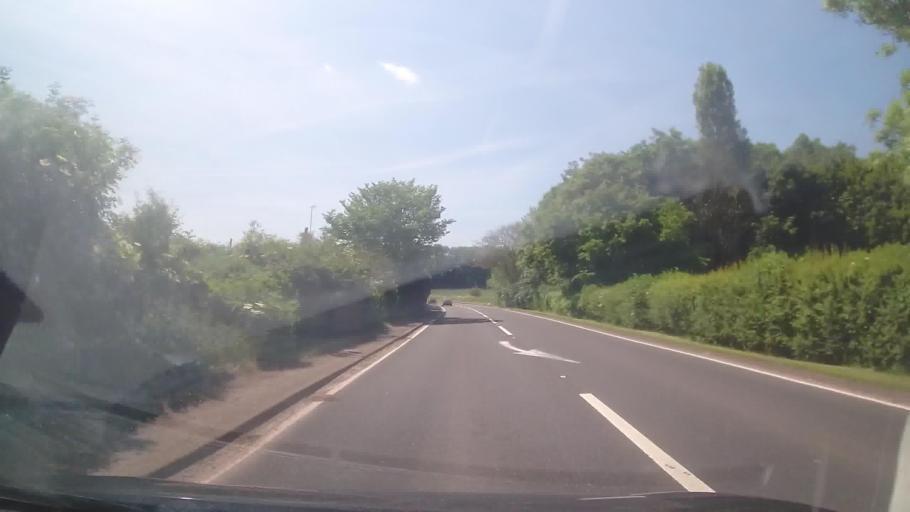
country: GB
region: England
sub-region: Herefordshire
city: Wellington
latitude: 52.1198
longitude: -2.7322
